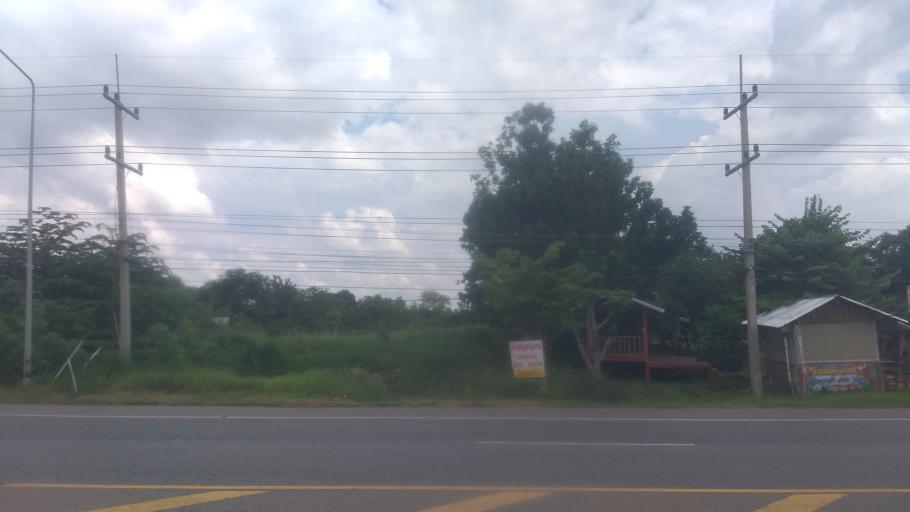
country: TH
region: Chaiyaphum
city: Noen Sa-nga
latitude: 15.6764
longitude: 101.9825
